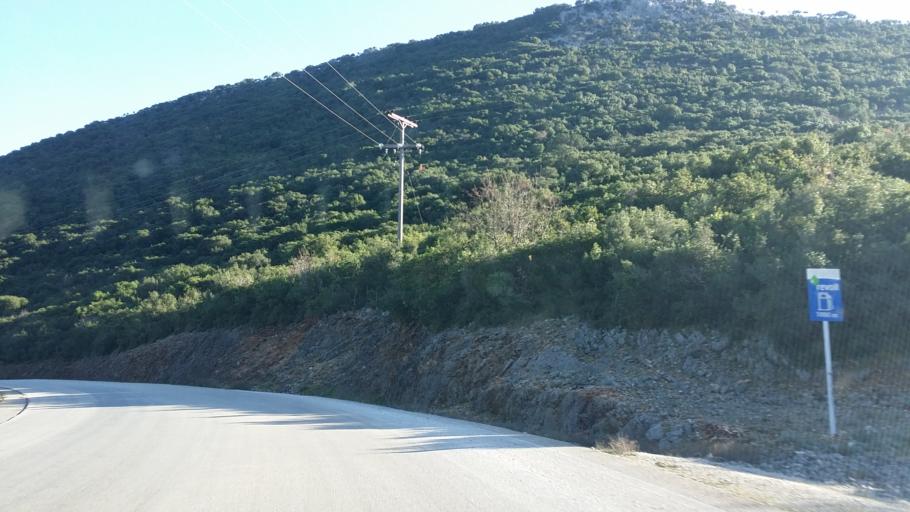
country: GR
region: West Greece
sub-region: Nomos Aitolias kai Akarnanias
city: Astakos
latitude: 38.6079
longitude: 21.1278
